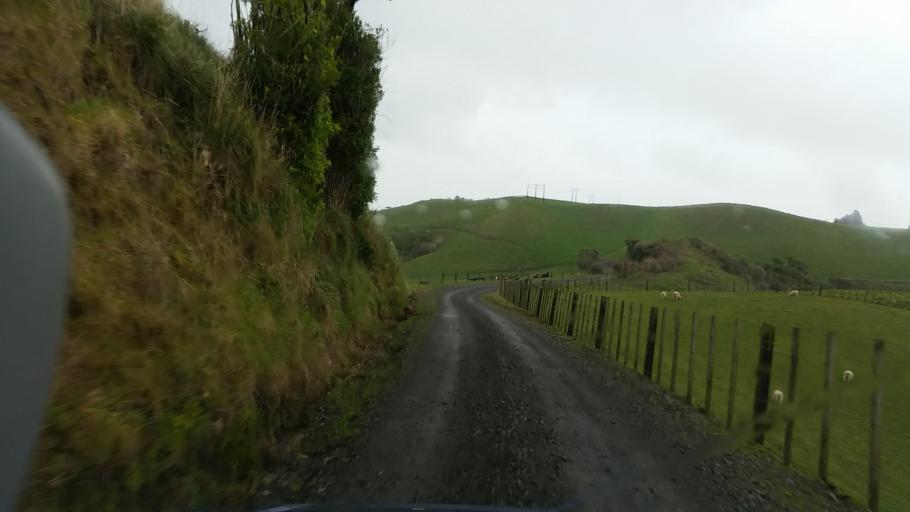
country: NZ
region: Taranaki
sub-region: South Taranaki District
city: Eltham
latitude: -39.2780
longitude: 174.3384
